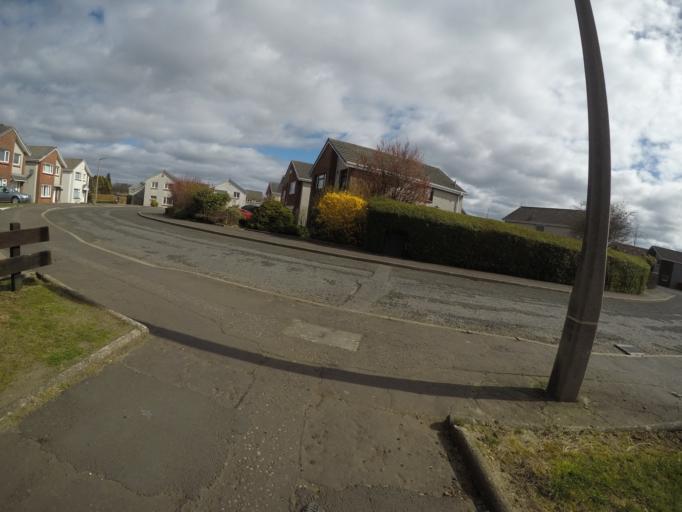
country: GB
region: Scotland
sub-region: South Ayrshire
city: Troon
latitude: 55.5656
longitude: -4.6429
